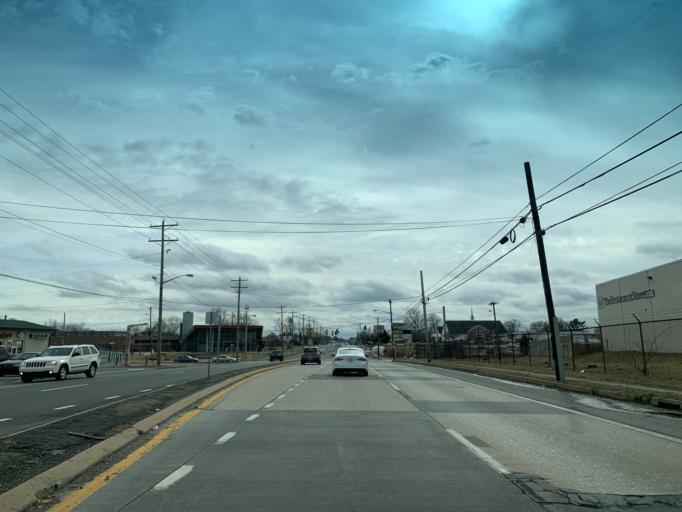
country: US
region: Delaware
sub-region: New Castle County
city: Wilmington Manor
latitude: 39.7038
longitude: -75.5510
